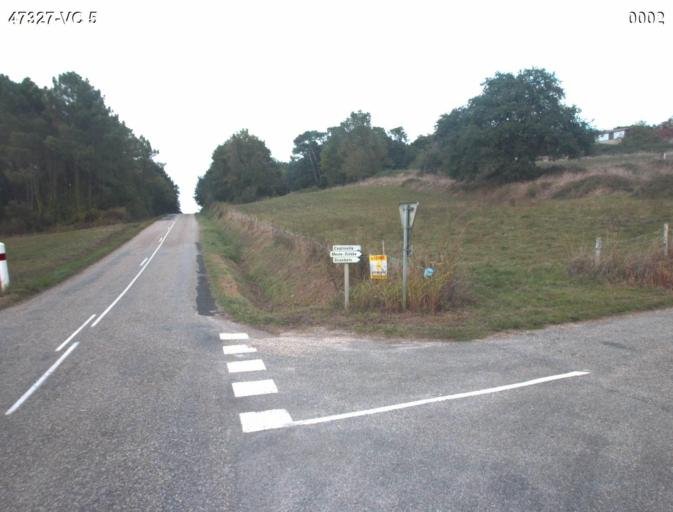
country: FR
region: Aquitaine
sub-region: Departement du Lot-et-Garonne
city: Buzet-sur-Baise
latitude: 44.2198
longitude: 0.2698
